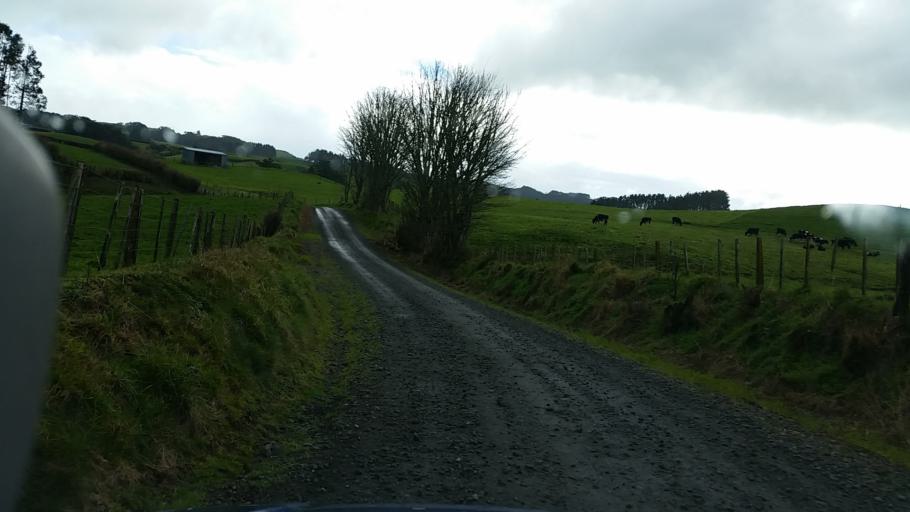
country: NZ
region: Taranaki
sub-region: South Taranaki District
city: Eltham
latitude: -39.2829
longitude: 174.3379
